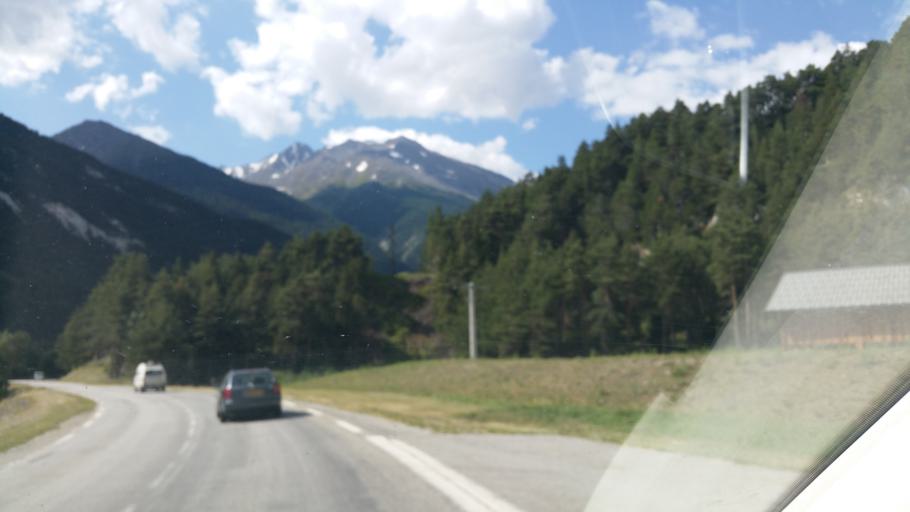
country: FR
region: Rhone-Alpes
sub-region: Departement de la Savoie
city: Modane
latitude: 45.2430
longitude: 6.7923
